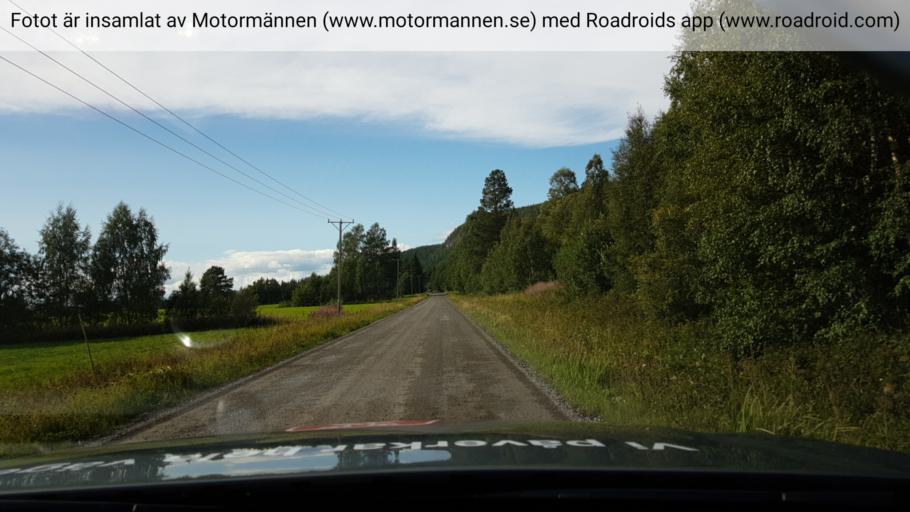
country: SE
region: Jaemtland
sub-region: Braecke Kommun
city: Braecke
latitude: 63.2039
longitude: 15.4111
